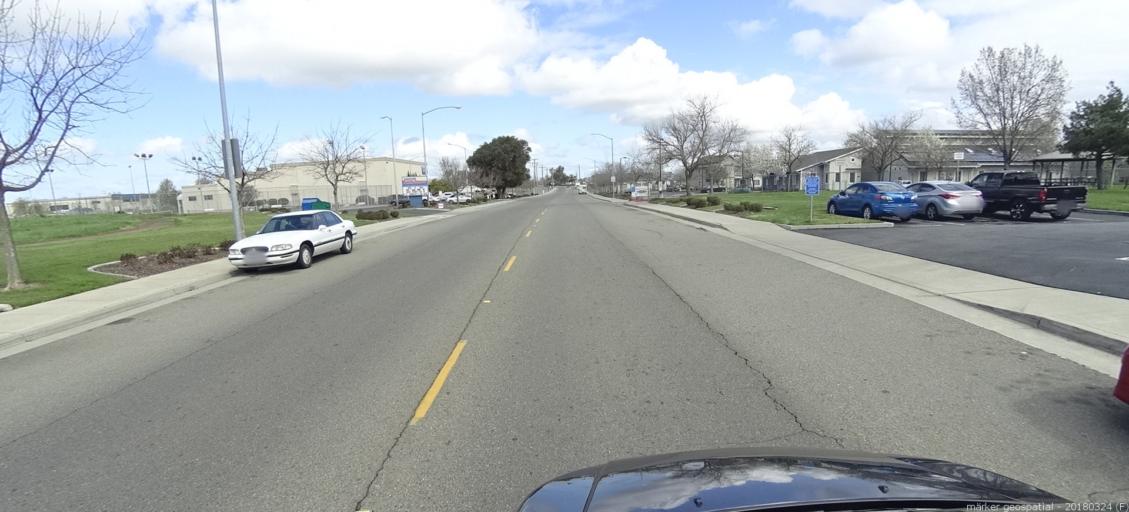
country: US
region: California
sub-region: Sacramento County
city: North Highlands
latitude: 38.6723
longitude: -121.3875
